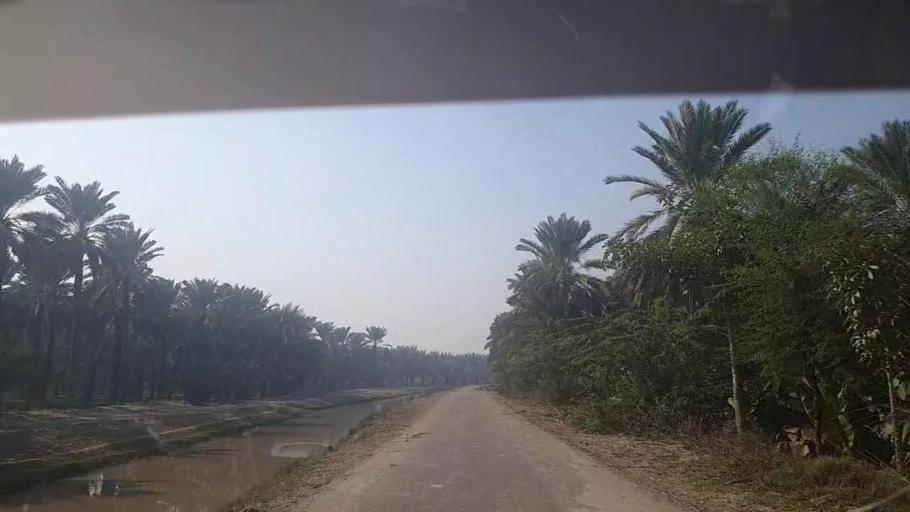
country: PK
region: Sindh
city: Khairpur
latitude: 27.4661
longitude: 68.7149
